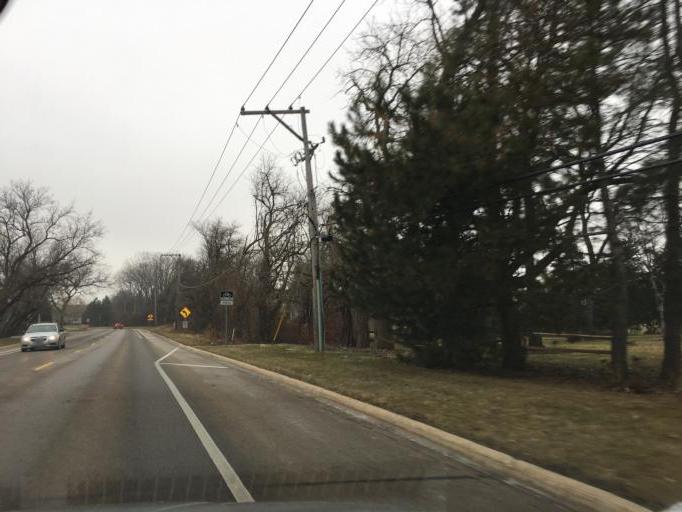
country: US
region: Illinois
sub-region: McHenry County
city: Lakewood
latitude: 42.2190
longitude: -88.3469
